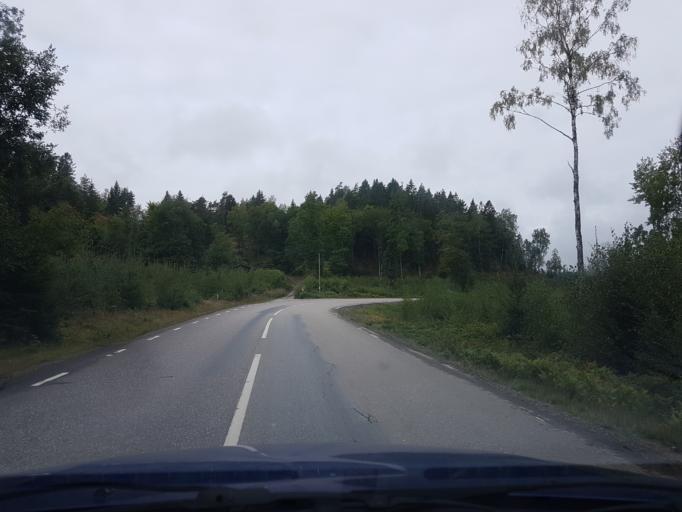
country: SE
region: Vaestra Goetaland
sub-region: Ale Kommun
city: Salanda
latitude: 57.9385
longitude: 12.2471
